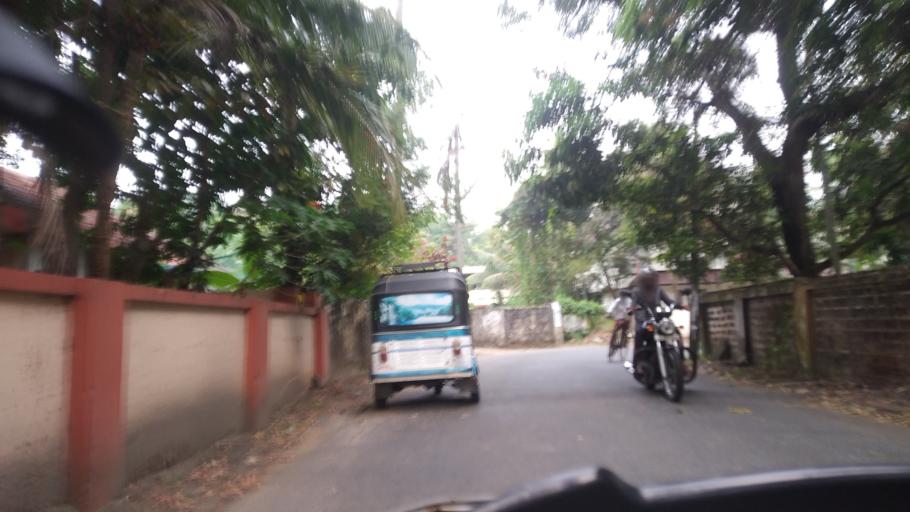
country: IN
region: Kerala
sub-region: Thrissur District
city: Kodungallur
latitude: 10.1452
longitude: 76.2363
